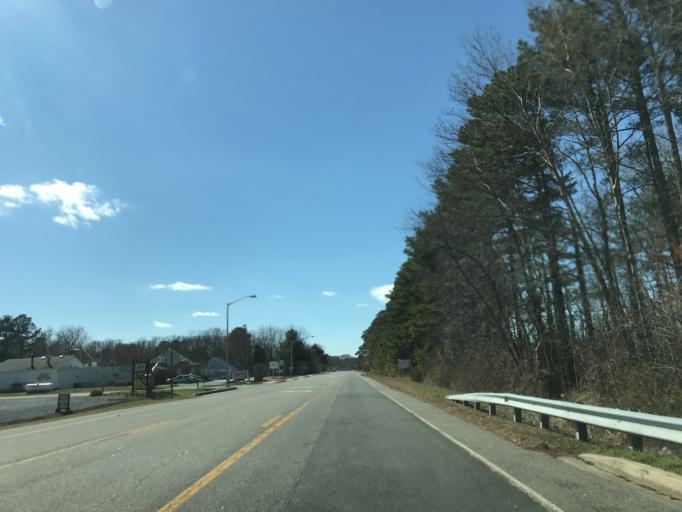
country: US
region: Maryland
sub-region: Kent County
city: Rock Hall
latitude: 39.1391
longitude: -76.2282
